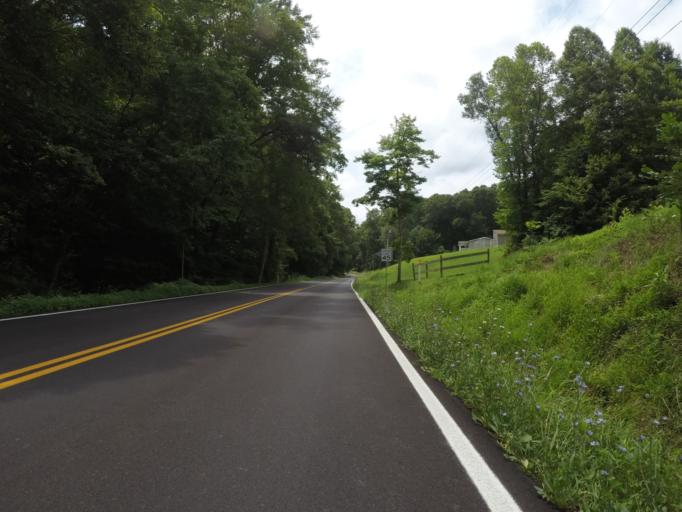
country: US
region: Kentucky
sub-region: Boyd County
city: Catlettsburg
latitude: 38.4337
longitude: -82.6282
